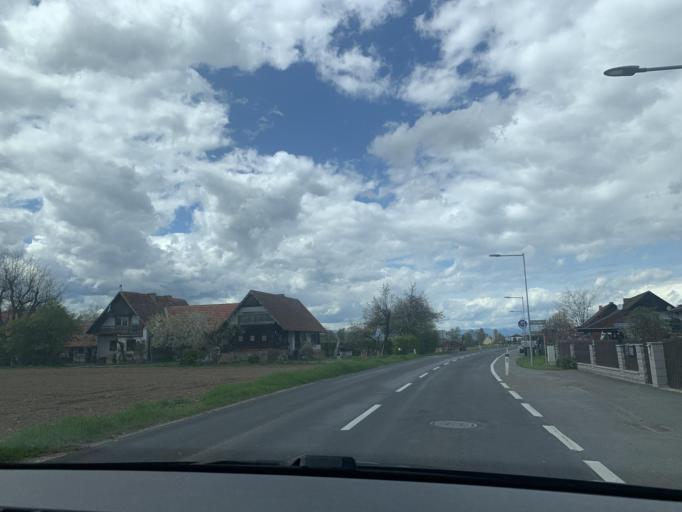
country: AT
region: Styria
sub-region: Politischer Bezirk Graz-Umgebung
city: Zettling
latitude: 46.9231
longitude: 15.3967
